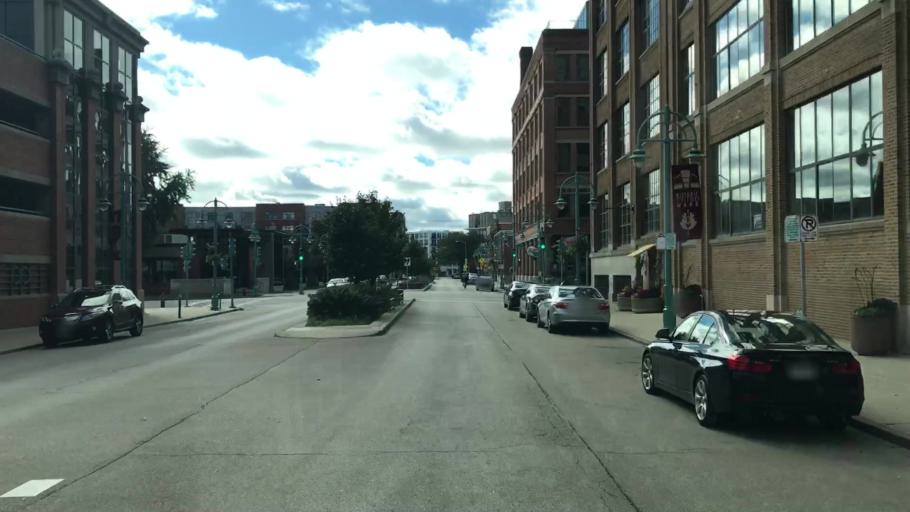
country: US
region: Wisconsin
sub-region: Milwaukee County
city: Milwaukee
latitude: 43.0333
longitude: -87.9059
